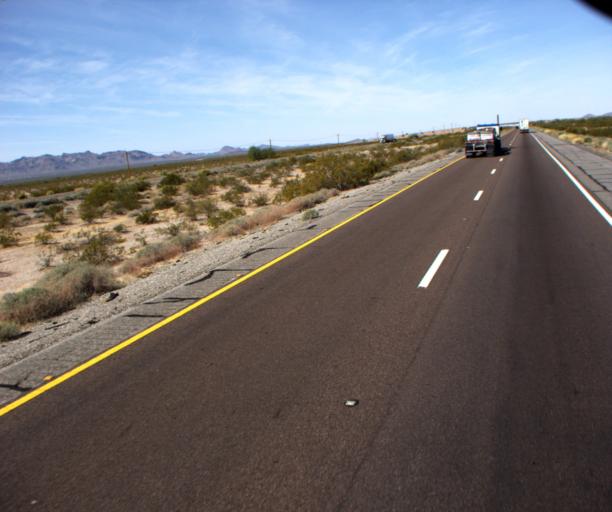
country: US
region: Arizona
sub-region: La Paz County
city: Salome
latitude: 33.5597
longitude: -113.2897
